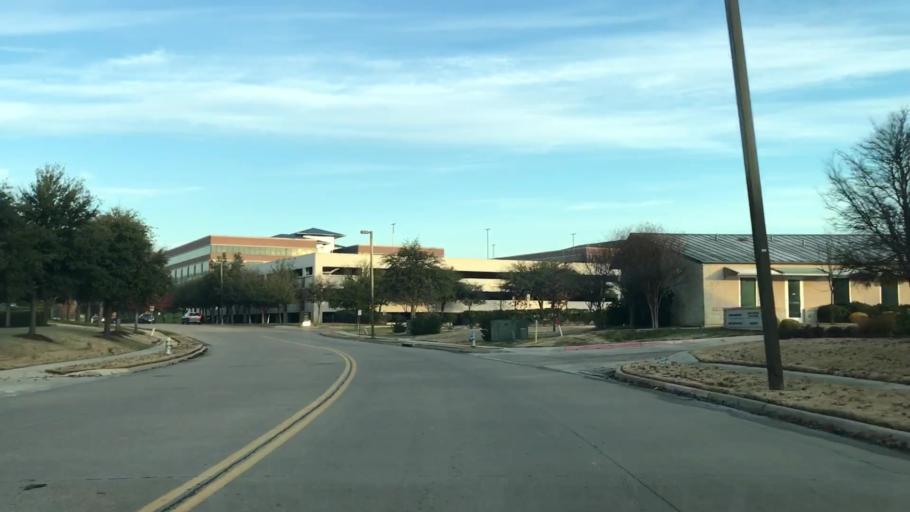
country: US
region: Texas
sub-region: Dallas County
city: Farmers Branch
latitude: 32.8970
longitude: -96.9624
